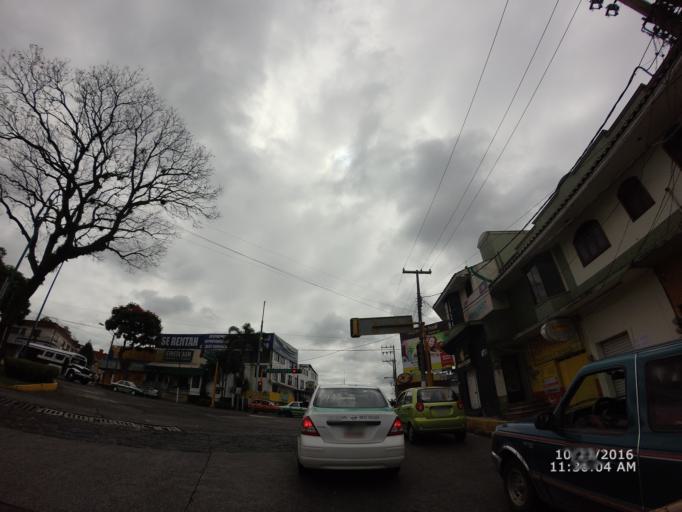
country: MX
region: Veracruz
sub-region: Xalapa
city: Xalapa de Enriquez
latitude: 19.5369
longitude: -96.9307
